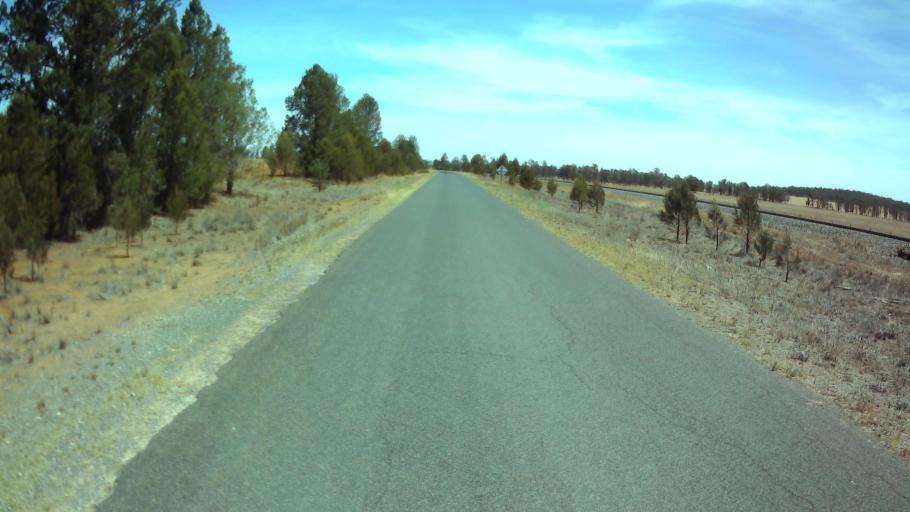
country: AU
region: New South Wales
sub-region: Weddin
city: Grenfell
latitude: -33.7750
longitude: 147.7552
